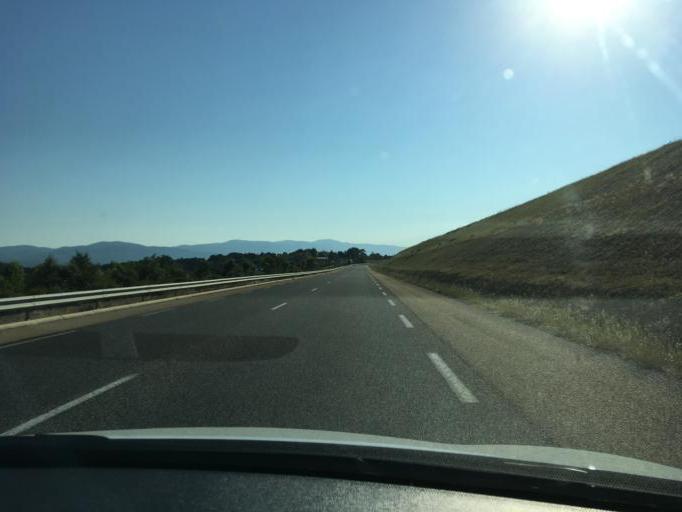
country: FR
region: Provence-Alpes-Cote d'Azur
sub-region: Departement des Bouches-du-Rhone
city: Charleval
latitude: 43.7170
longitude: 5.2572
